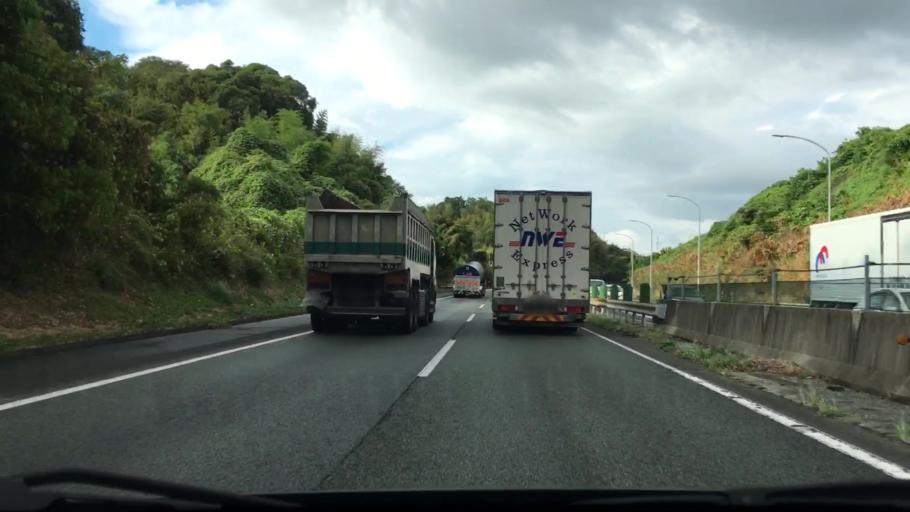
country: JP
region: Fukuoka
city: Nishifukuma
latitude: 33.7457
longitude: 130.5272
